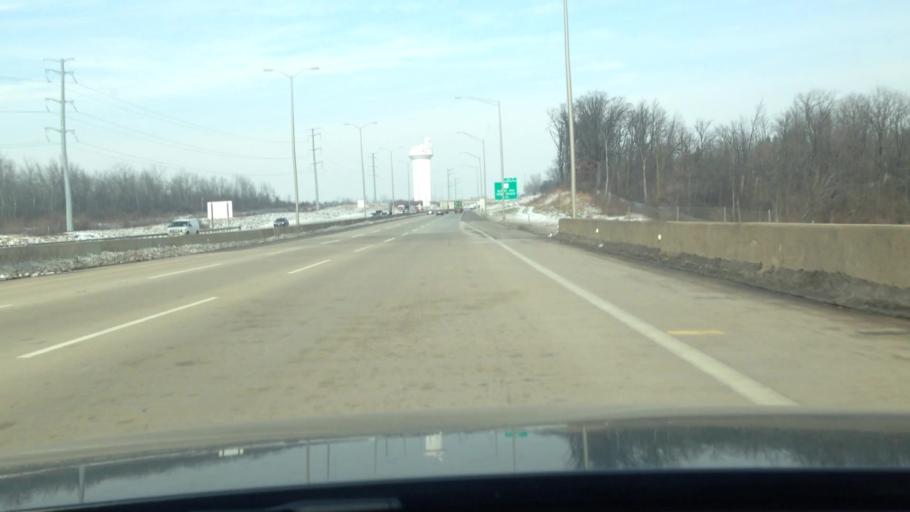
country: US
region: Illinois
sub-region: Will County
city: Lockport
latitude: 41.6053
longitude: -88.0124
